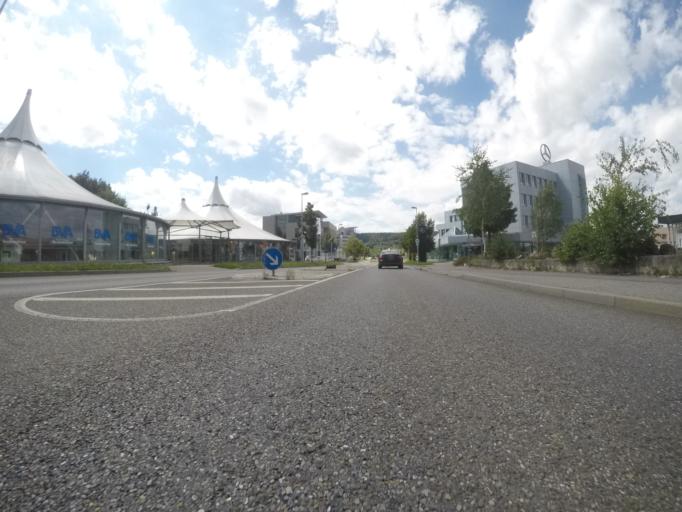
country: DE
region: Baden-Wuerttemberg
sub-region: Regierungsbezirk Stuttgart
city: Leonberg
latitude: 48.7859
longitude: 9.0209
